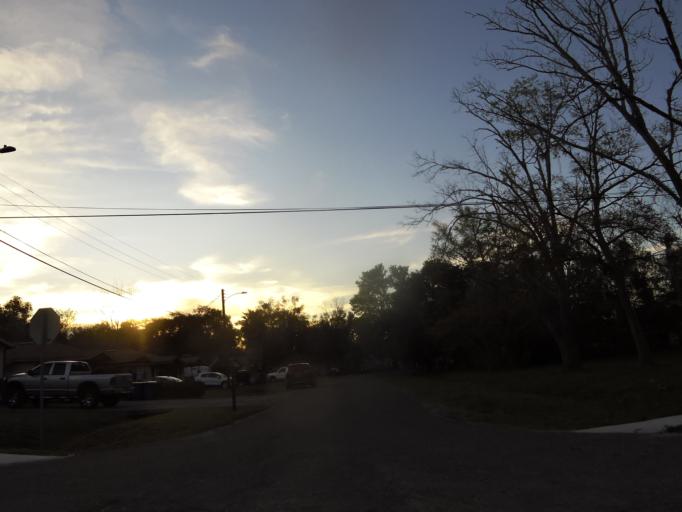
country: US
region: Florida
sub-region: Duval County
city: Jacksonville
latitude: 30.4656
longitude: -81.6309
